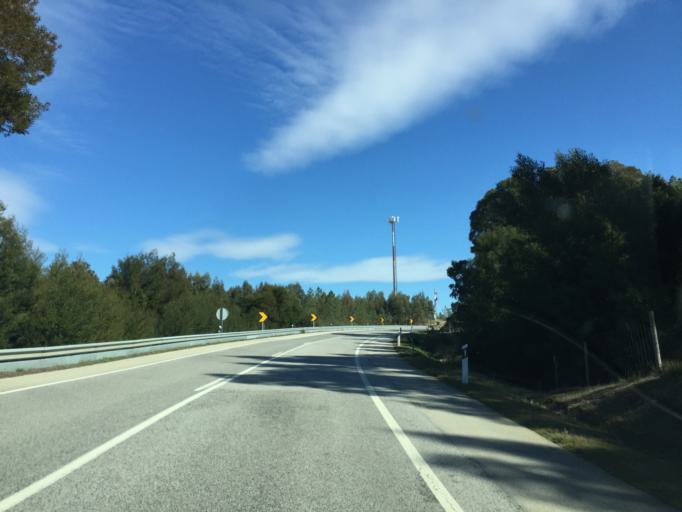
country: ES
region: Extremadura
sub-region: Provincia de Caceres
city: Cedillo
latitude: 39.7314
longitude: -7.6782
